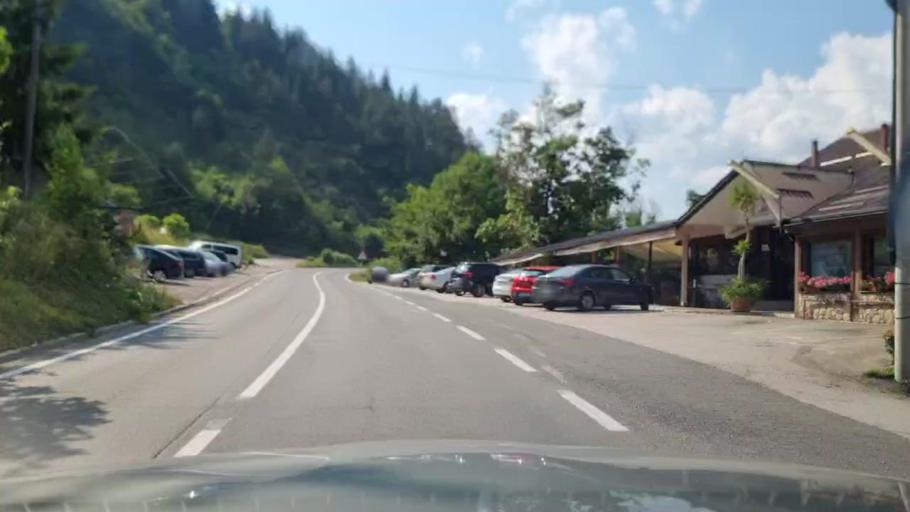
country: BA
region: Federation of Bosnia and Herzegovina
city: Olovo
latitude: 44.1184
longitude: 18.5814
